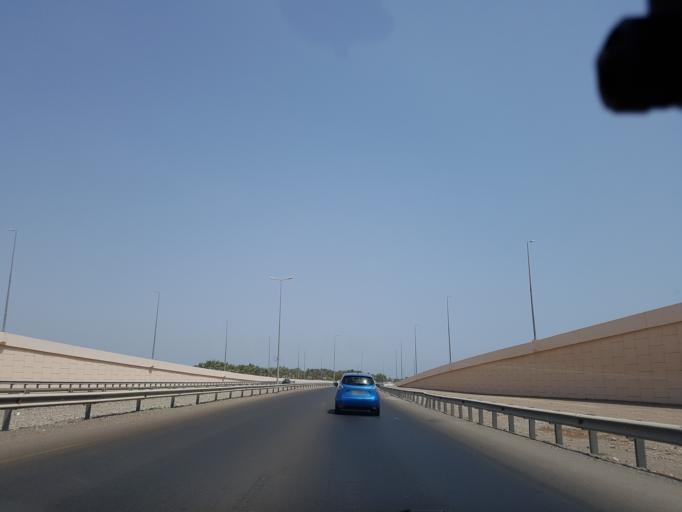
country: OM
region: Al Batinah
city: Saham
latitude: 24.1810
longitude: 56.8564
